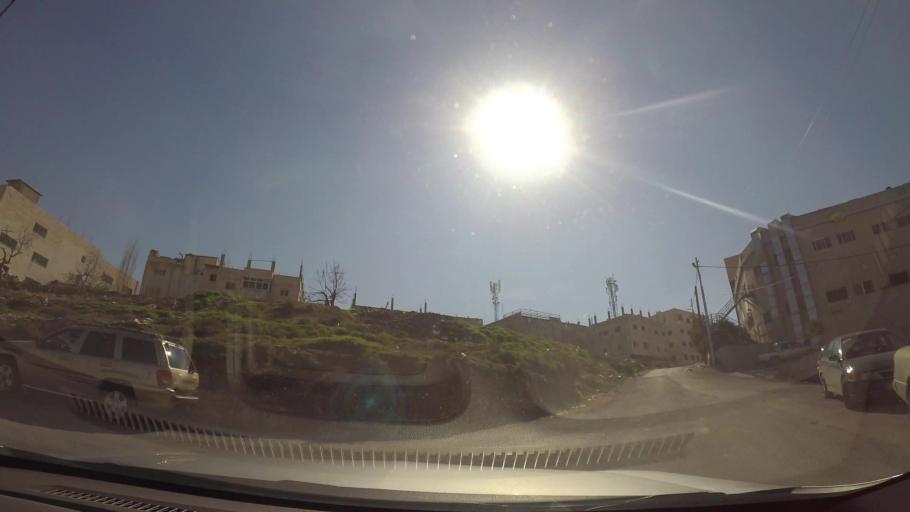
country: JO
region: Amman
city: Al Bunayyat ash Shamaliyah
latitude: 31.9094
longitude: 35.9023
